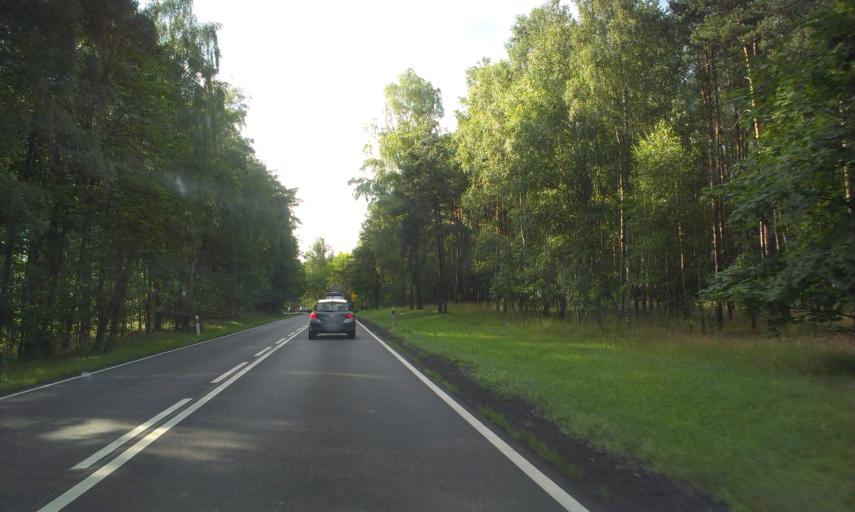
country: PL
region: Greater Poland Voivodeship
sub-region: Powiat zlotowski
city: Okonek
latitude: 53.4976
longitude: 16.8577
